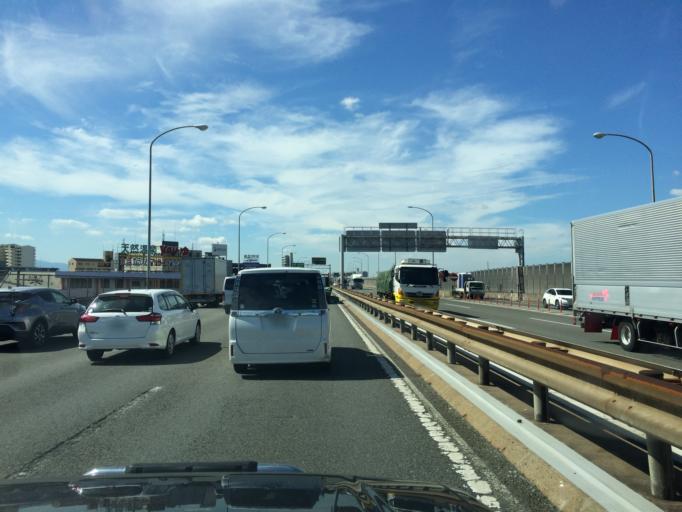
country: JP
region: Osaka
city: Matsubara
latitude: 34.5855
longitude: 135.5714
